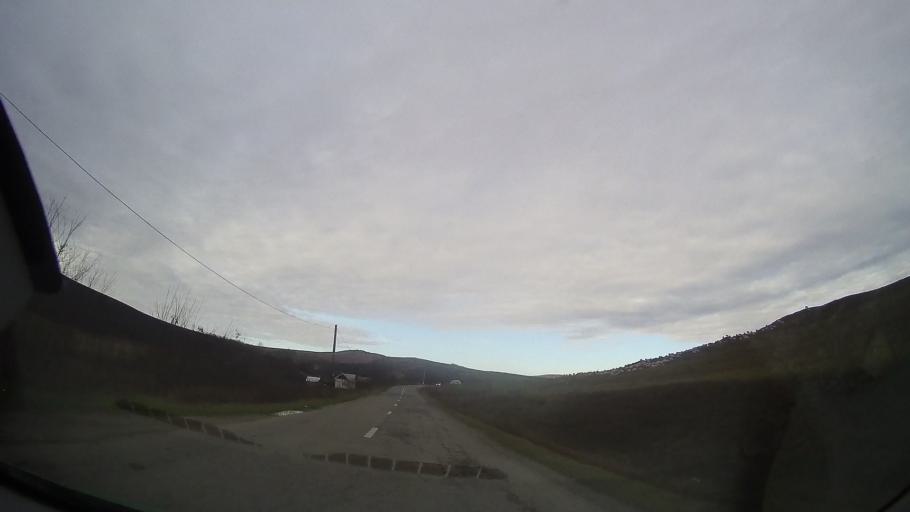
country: RO
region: Cluj
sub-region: Comuna Camarasu
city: Camarasu
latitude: 46.8130
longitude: 24.1425
